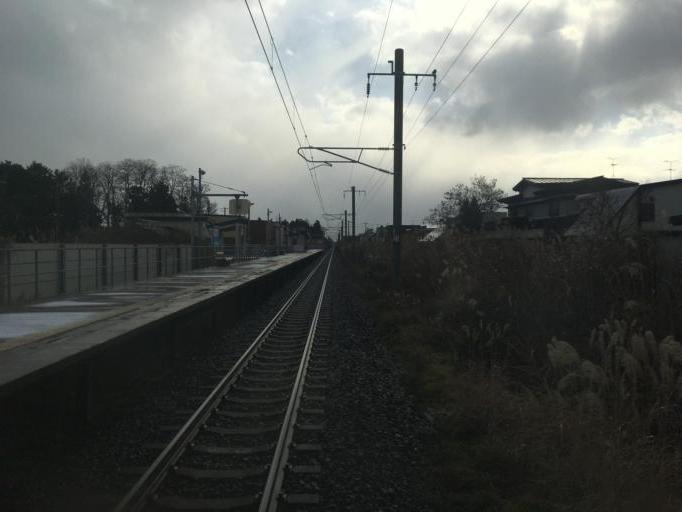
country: JP
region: Aomori
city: Aomori Shi
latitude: 40.8571
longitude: 140.6901
